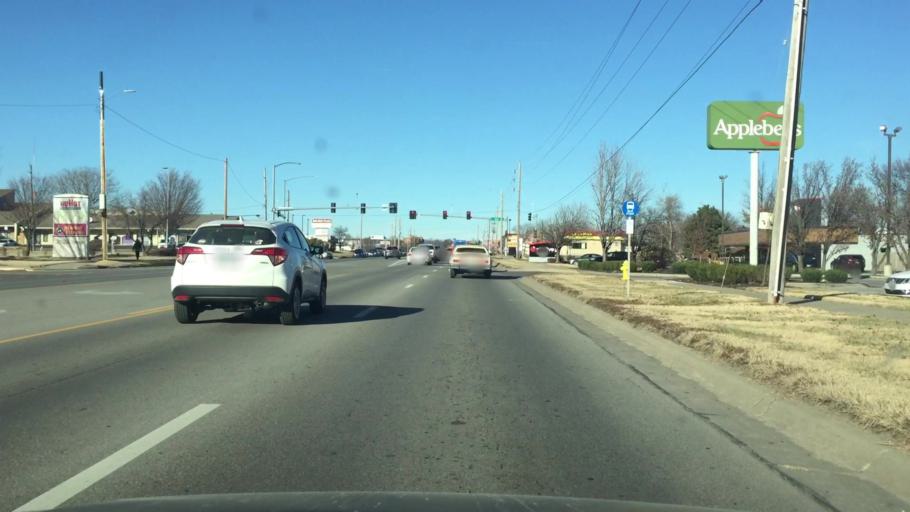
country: US
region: Kansas
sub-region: Douglas County
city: Lawrence
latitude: 38.9375
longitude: -95.2605
